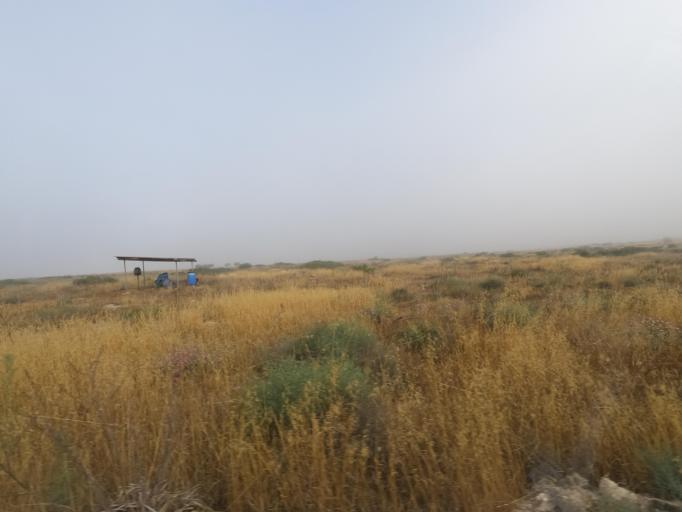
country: CY
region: Ammochostos
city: Acheritou
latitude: 35.1046
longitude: 33.8769
